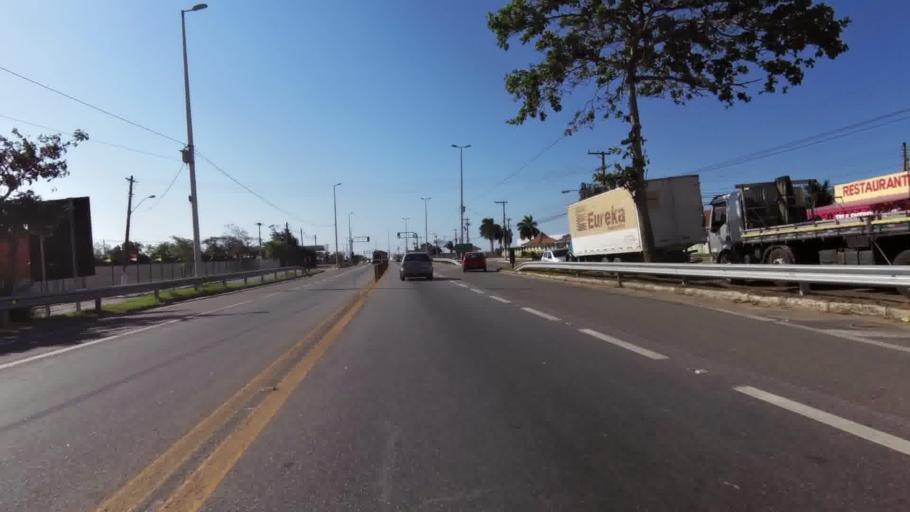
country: BR
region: Rio de Janeiro
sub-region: Campos Dos Goytacazes
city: Campos
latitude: -21.7107
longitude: -41.3086
